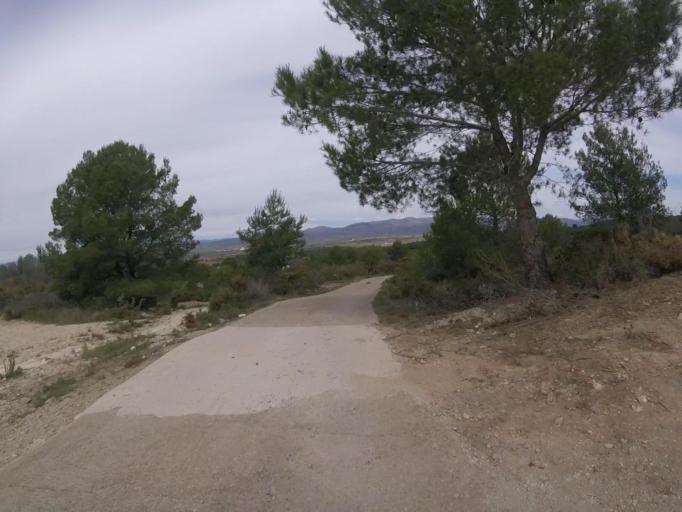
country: ES
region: Valencia
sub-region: Provincia de Castello
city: Cabanes
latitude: 40.1920
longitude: 0.0766
